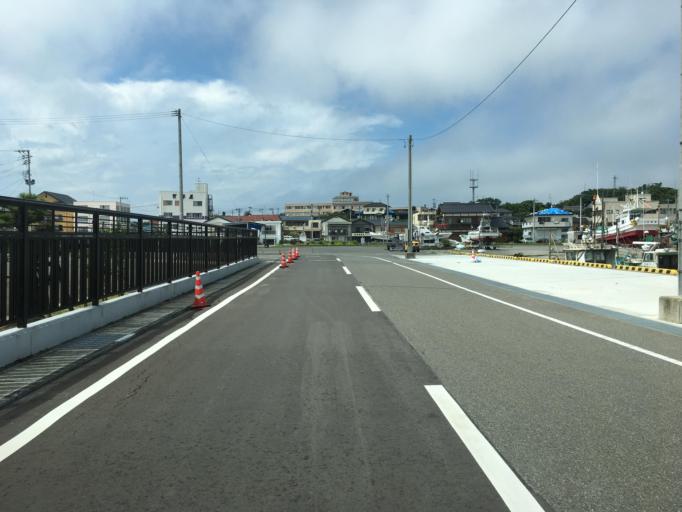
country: JP
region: Miyagi
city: Marumori
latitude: 37.8213
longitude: 140.9693
